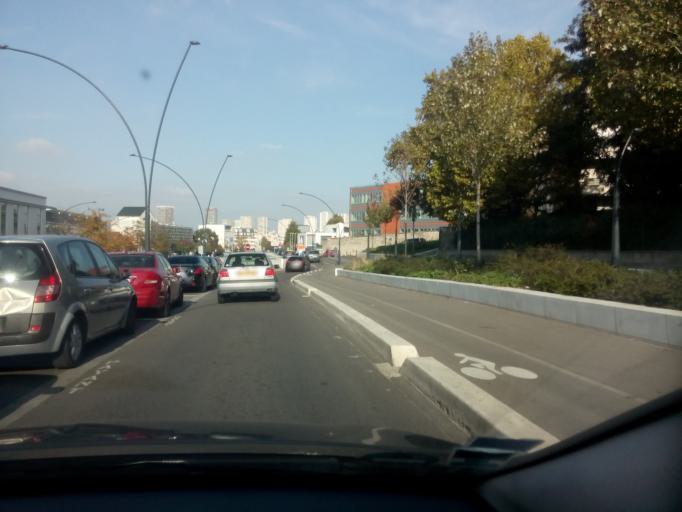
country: FR
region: Ile-de-France
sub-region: Departement du Val-de-Marne
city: Gentilly
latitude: 48.8092
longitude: 2.3488
